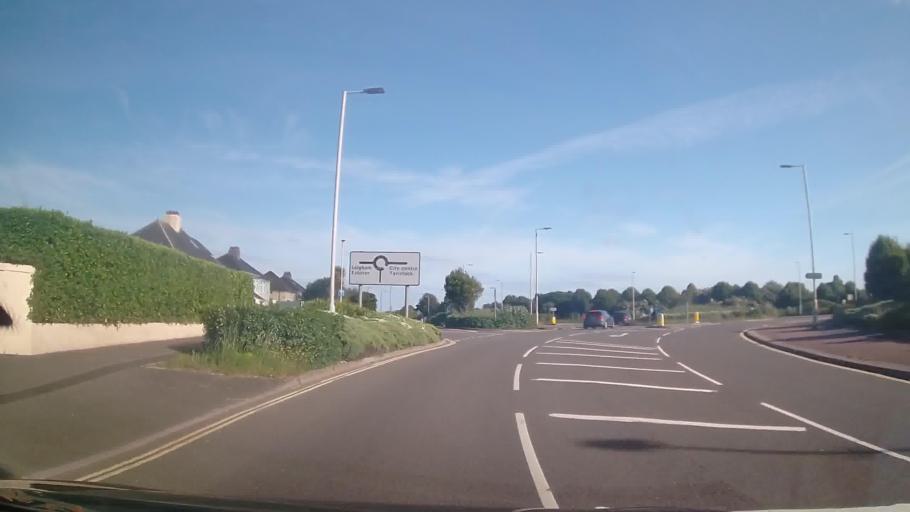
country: GB
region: England
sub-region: Devon
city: Plympton
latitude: 50.4270
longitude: -4.1092
